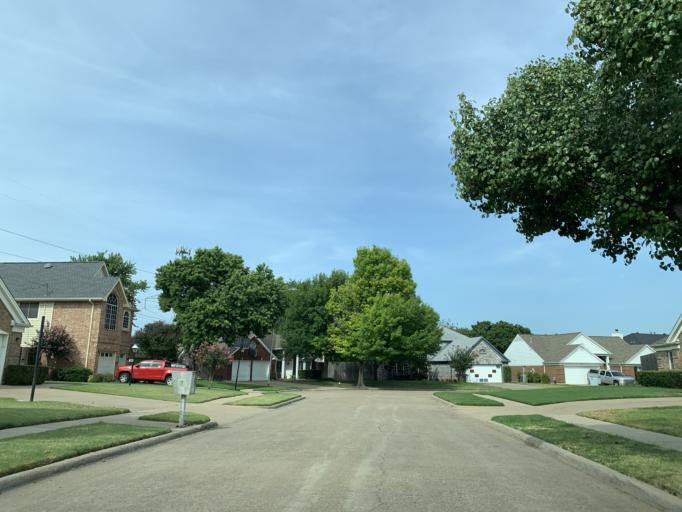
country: US
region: Texas
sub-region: Dallas County
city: Grand Prairie
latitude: 32.6619
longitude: -97.0086
